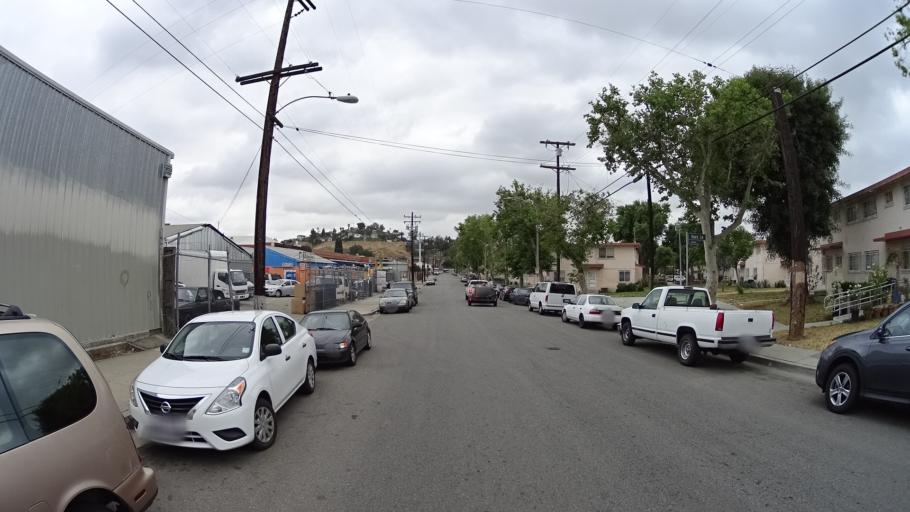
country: US
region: California
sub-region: Los Angeles County
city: Boyle Heights
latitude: 34.0590
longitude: -118.1926
